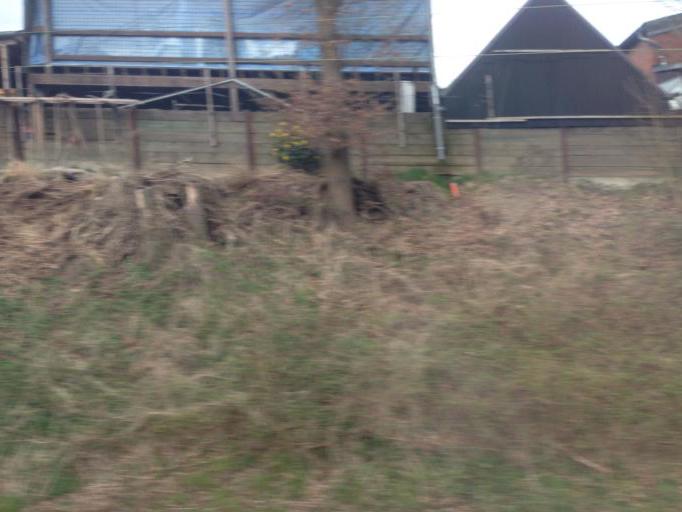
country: DE
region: North Rhine-Westphalia
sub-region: Regierungsbezirk Munster
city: Dulmen
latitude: 51.8321
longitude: 7.3042
